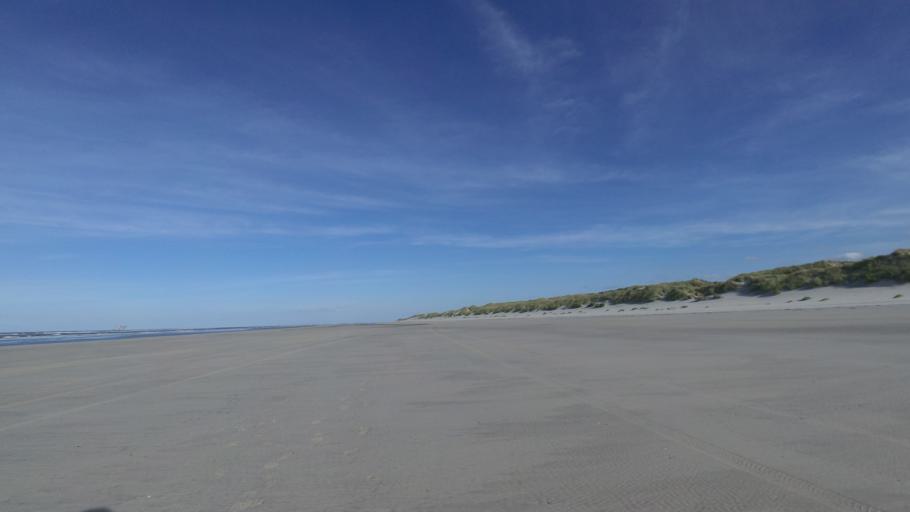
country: NL
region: Friesland
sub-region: Gemeente Dongeradeel
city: Holwerd
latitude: 53.4662
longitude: 5.8762
